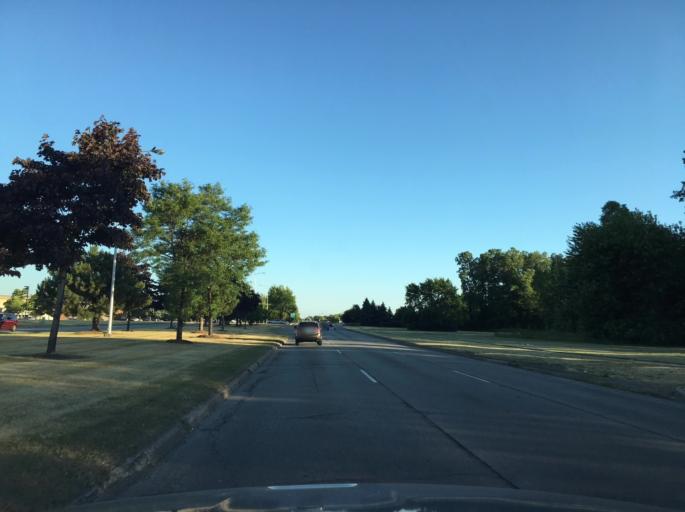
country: US
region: Michigan
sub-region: Macomb County
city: Utica
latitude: 42.6215
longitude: -82.9929
